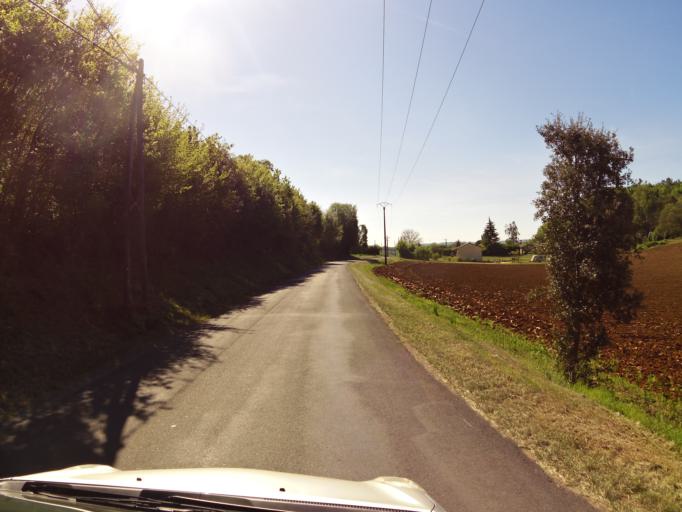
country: FR
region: Aquitaine
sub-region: Departement de la Dordogne
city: Carsac-Aillac
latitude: 44.8528
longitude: 1.2253
